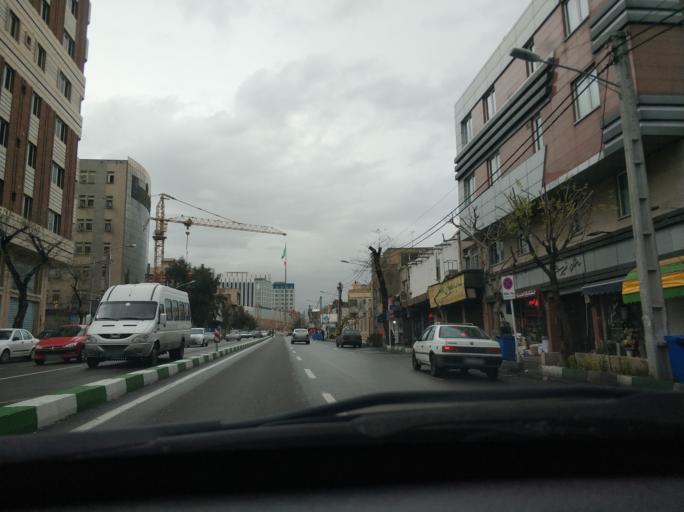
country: IR
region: Tehran
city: Tehran
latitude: 35.7041
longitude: 51.4394
